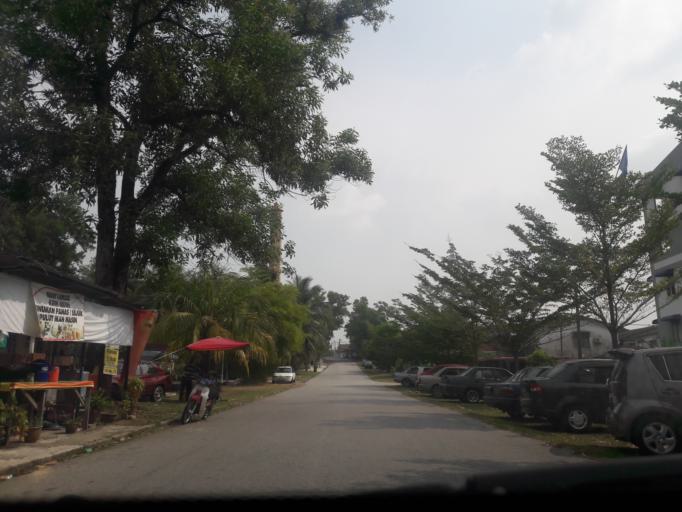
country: MY
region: Kedah
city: Kulim
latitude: 5.3617
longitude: 100.5377
